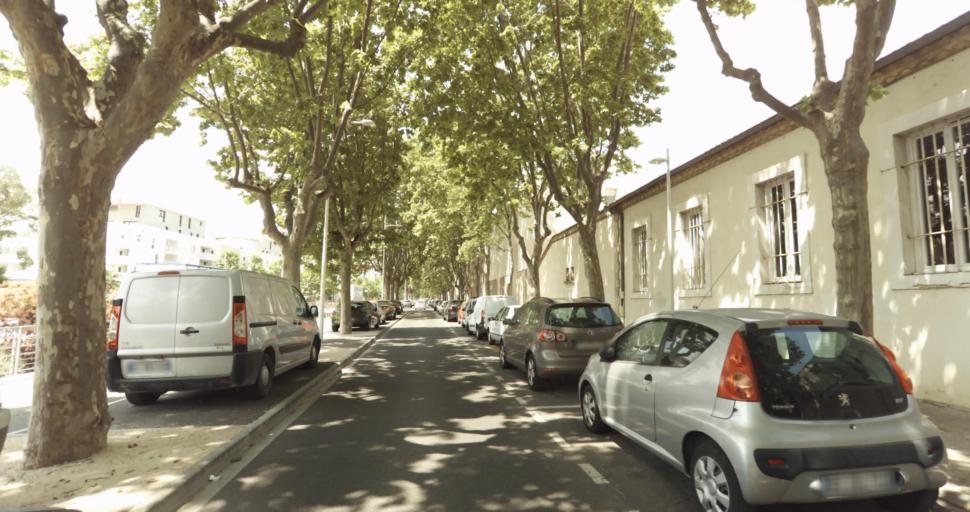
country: FR
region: Languedoc-Roussillon
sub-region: Departement du Gard
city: Nimes
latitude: 43.8459
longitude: 4.3709
